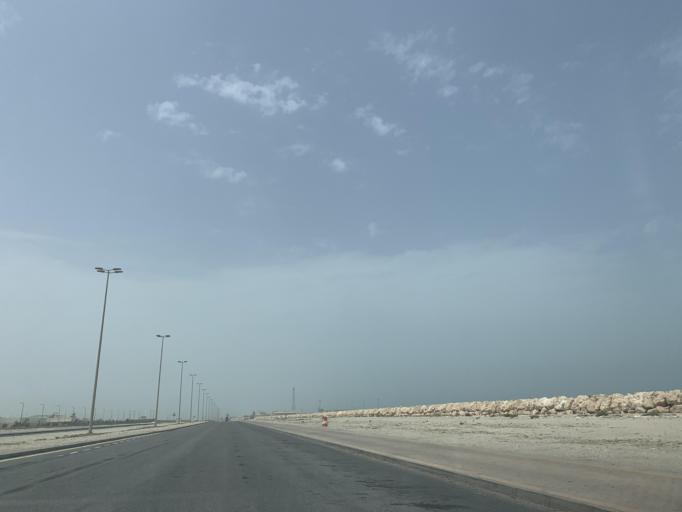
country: BH
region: Muharraq
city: Al Hadd
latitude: 26.2150
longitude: 50.7019
